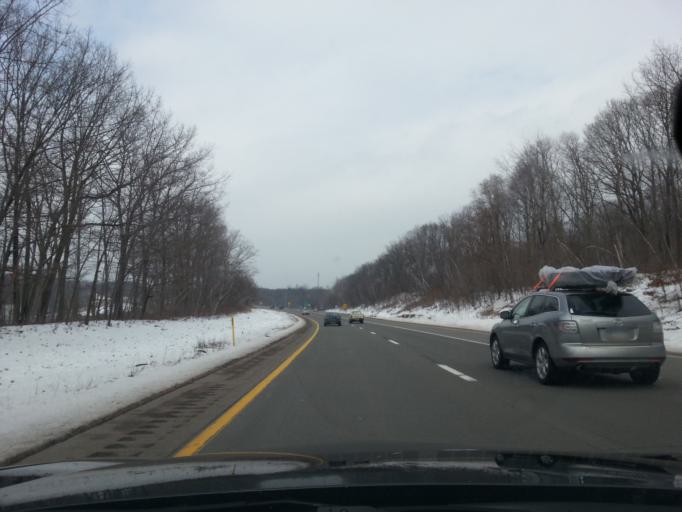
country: US
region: Pennsylvania
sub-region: Luzerne County
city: Freeland
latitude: 41.0790
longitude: -75.9664
